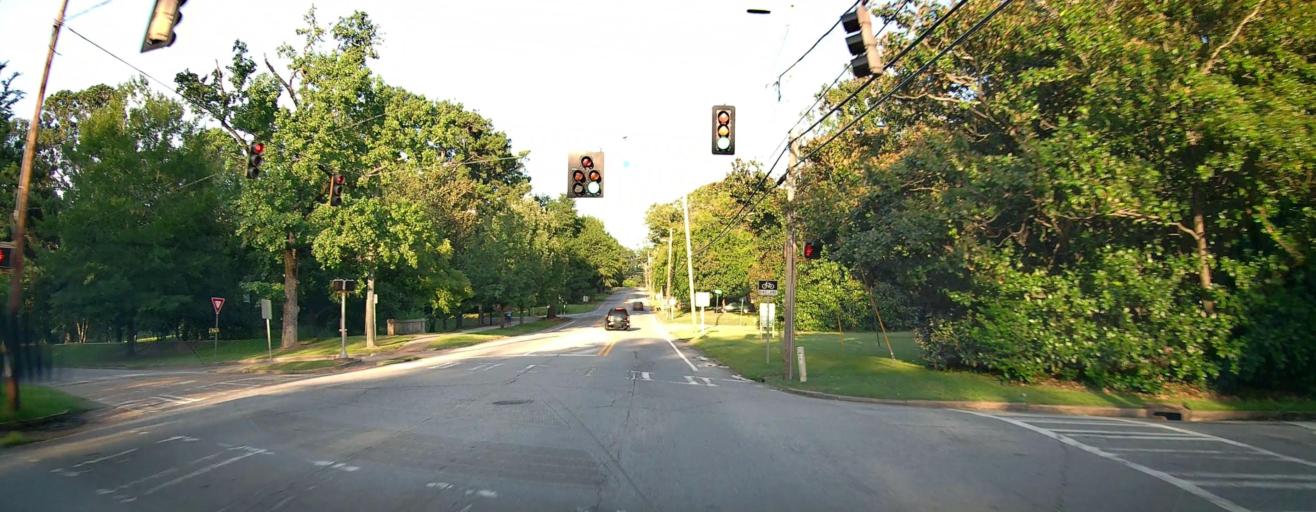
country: US
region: Georgia
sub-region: Muscogee County
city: Columbus
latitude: 32.4720
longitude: -84.9673
